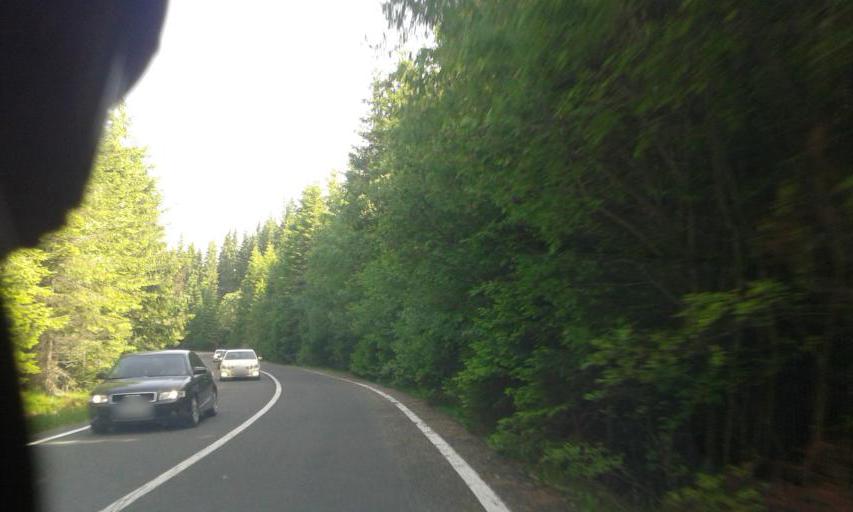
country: RO
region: Alba
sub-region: Comuna Sugag
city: Sugag
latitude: 45.5662
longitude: 23.6180
